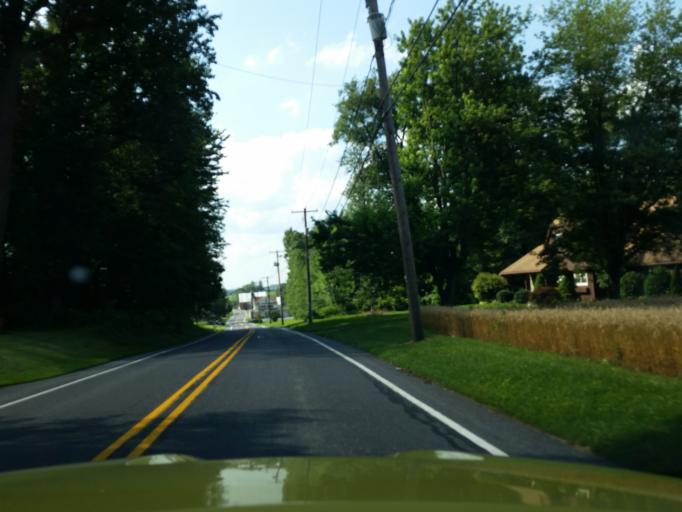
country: US
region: Pennsylvania
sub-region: Lancaster County
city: Manheim
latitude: 40.1726
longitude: -76.4550
